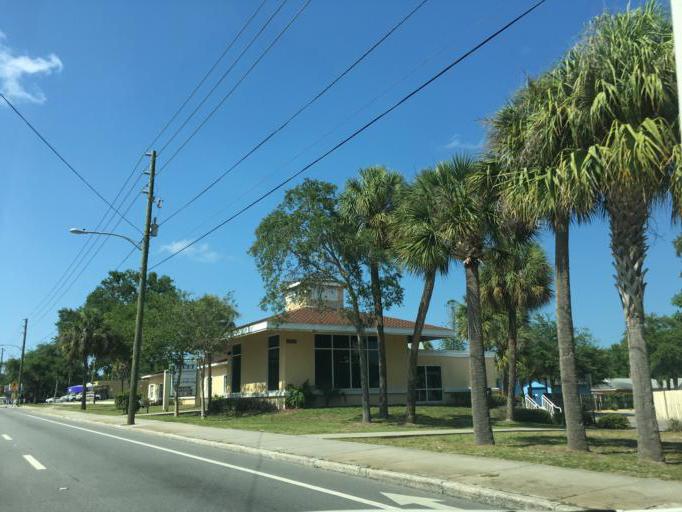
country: US
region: Florida
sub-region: Pinellas County
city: Saint Petersburg
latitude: 27.7541
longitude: -82.6466
